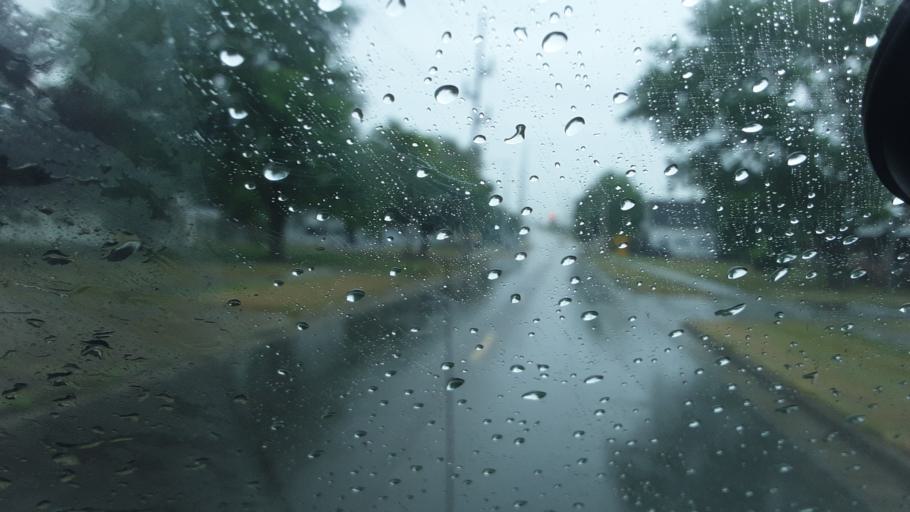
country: US
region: Ohio
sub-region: Williams County
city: Montpelier
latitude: 41.5752
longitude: -84.6070
